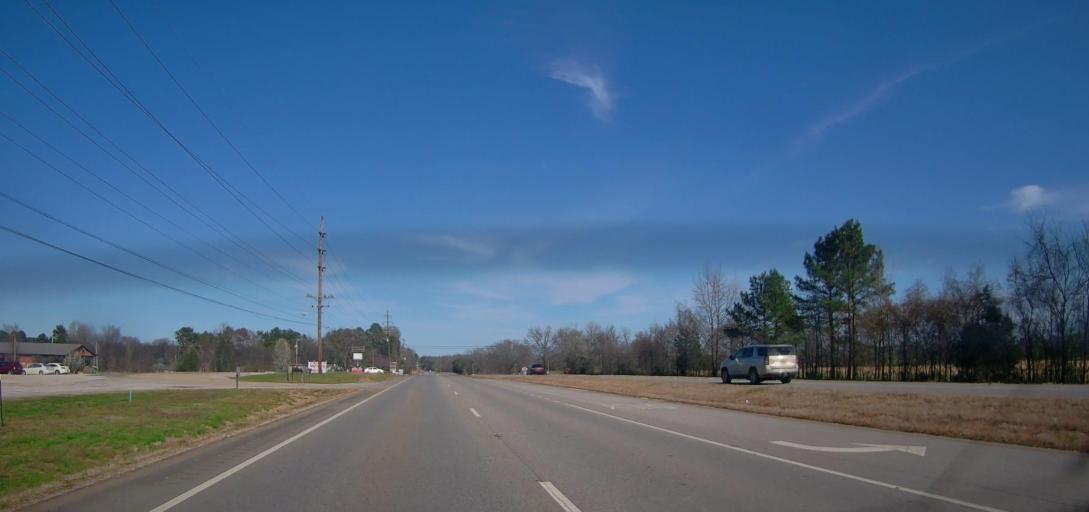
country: US
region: Alabama
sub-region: Lauderdale County
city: Killen
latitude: 34.8598
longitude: -87.4983
